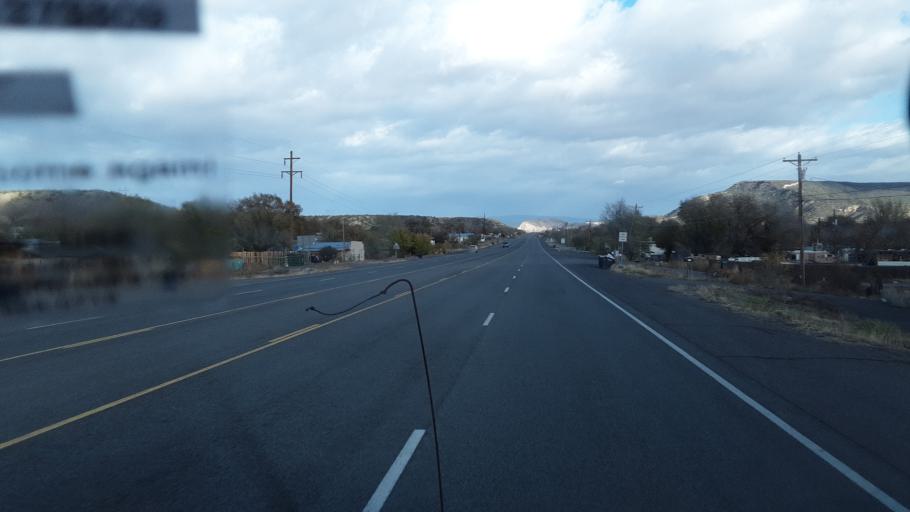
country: US
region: New Mexico
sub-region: Rio Arriba County
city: Ohkay Owingeh
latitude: 36.0551
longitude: -106.1158
